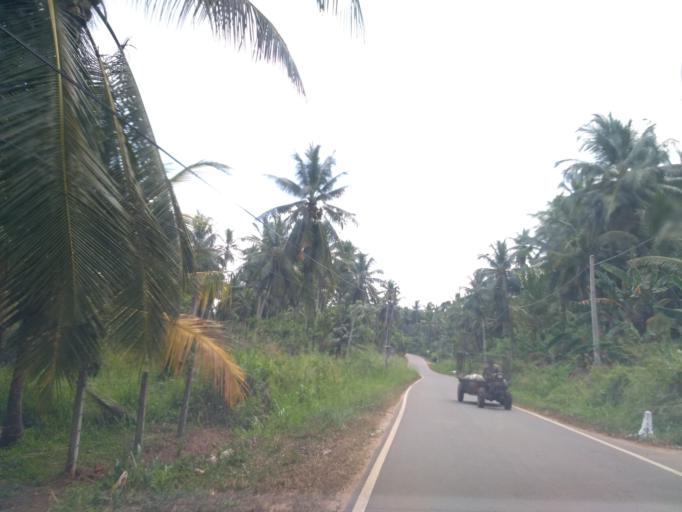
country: LK
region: North Western
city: Kuliyapitiya
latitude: 7.3363
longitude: 80.0618
